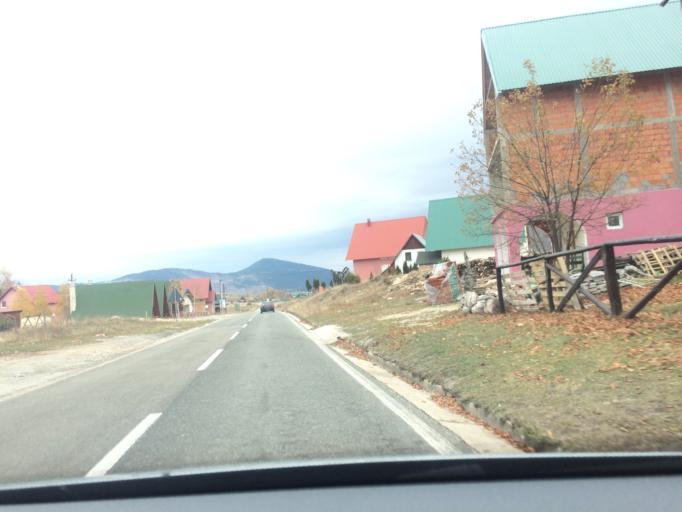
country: ME
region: Opstina Zabljak
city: Zabljak
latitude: 43.1632
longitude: 19.1449
